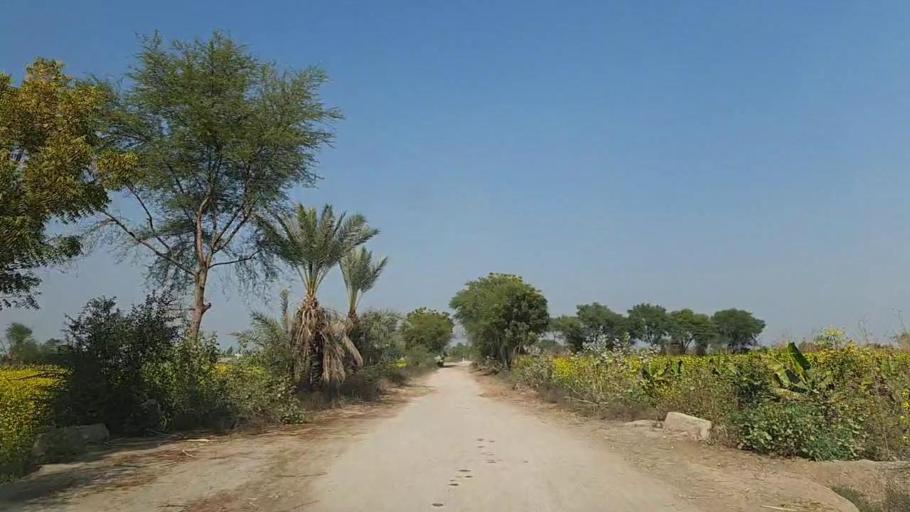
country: PK
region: Sindh
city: Daur
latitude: 26.4947
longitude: 68.2718
